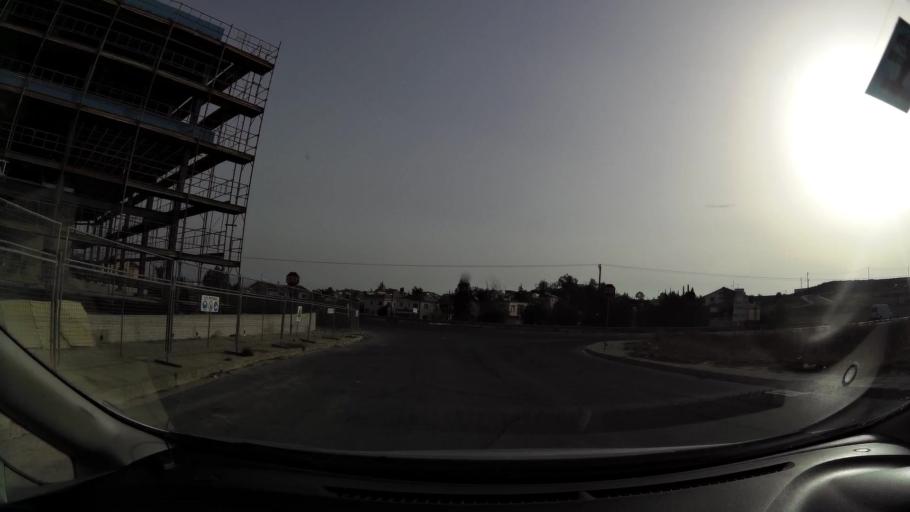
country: CY
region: Lefkosia
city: Dali
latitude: 35.0632
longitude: 33.3864
